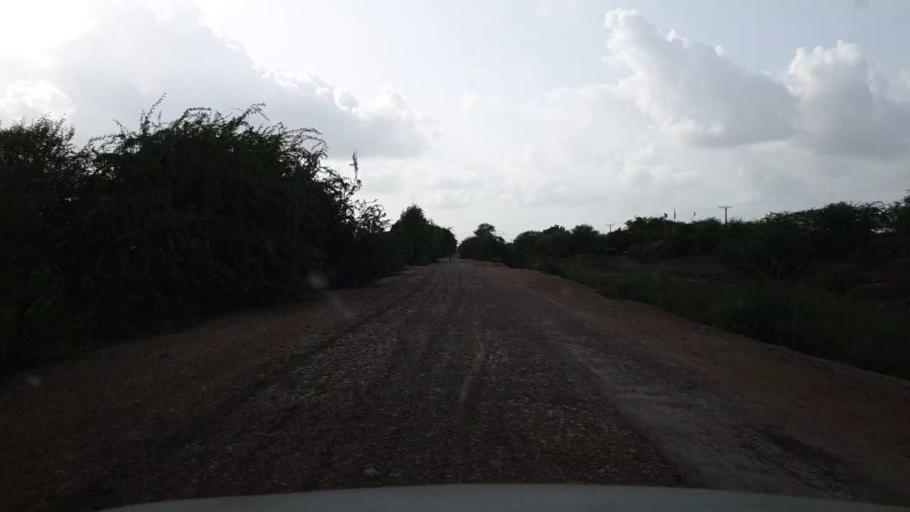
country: PK
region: Sindh
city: Kario
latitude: 24.7649
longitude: 68.6014
